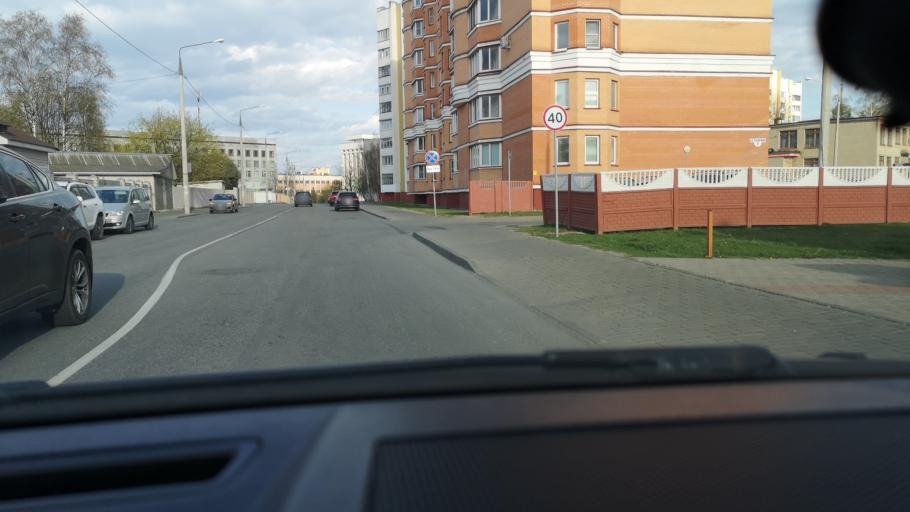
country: BY
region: Gomel
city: Gomel
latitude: 52.4428
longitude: 30.9973
